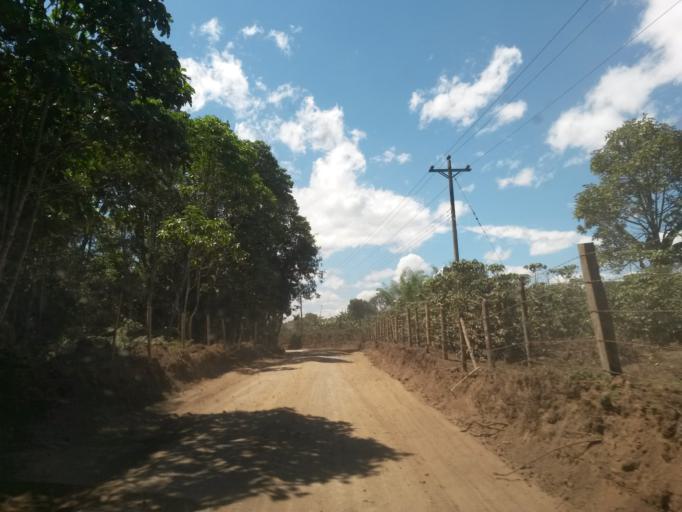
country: CO
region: Cauca
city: Morales
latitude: 2.7396
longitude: -76.6205
